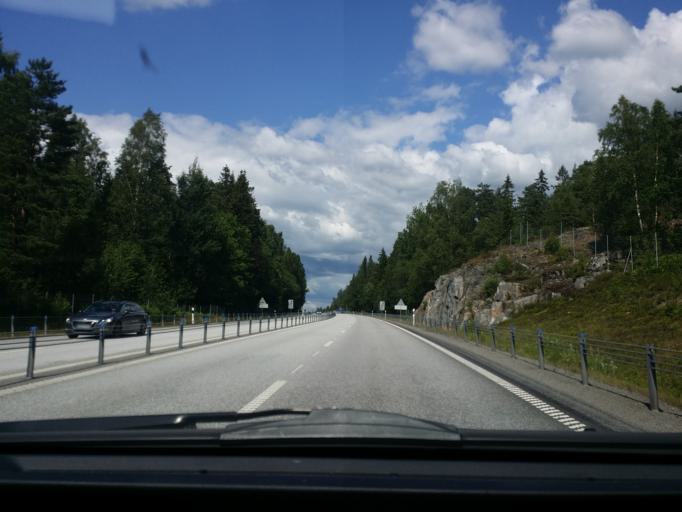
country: SE
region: OErebro
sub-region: Orebro Kommun
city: Hovsta
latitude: 59.3774
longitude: 15.2190
